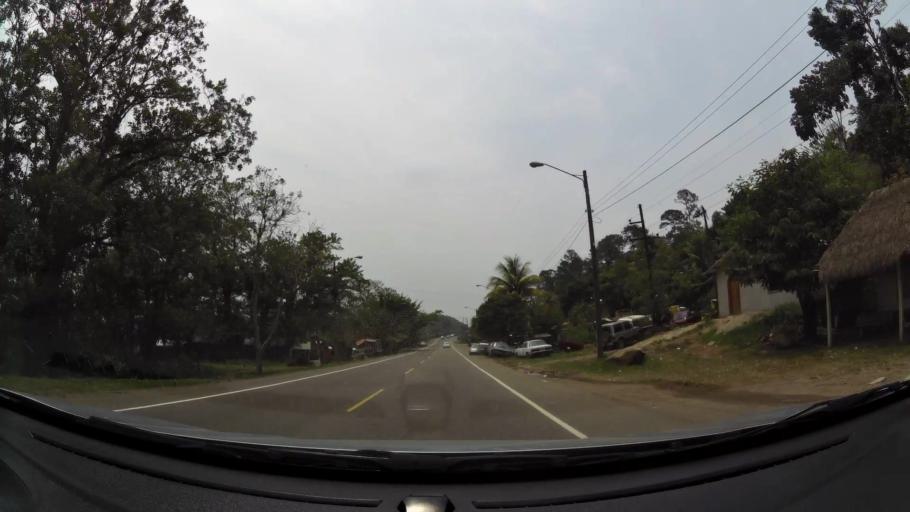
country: HN
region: Cortes
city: La Guama
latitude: 14.8906
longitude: -87.9402
